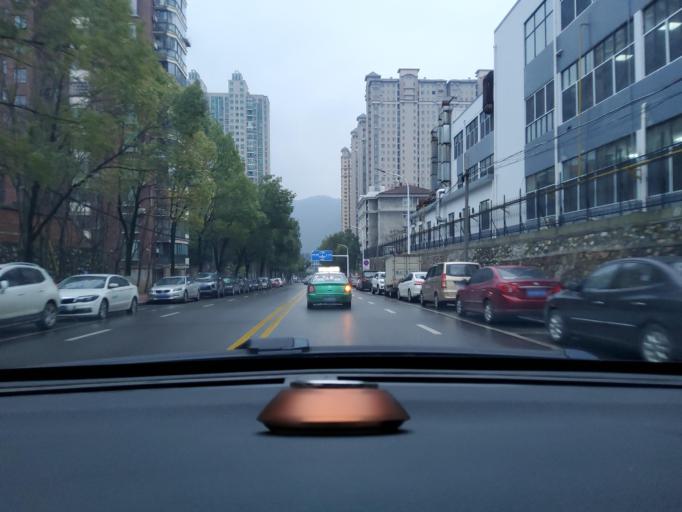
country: CN
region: Hubei
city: Tuanchengshan
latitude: 30.1912
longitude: 115.0275
